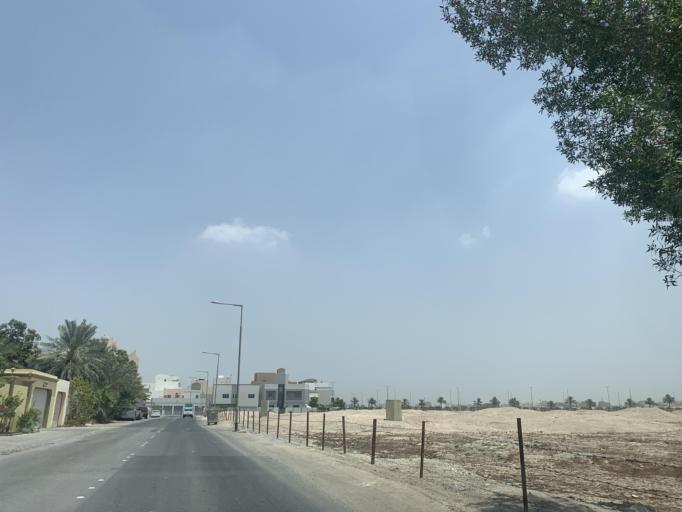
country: BH
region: Central Governorate
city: Madinat Hamad
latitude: 26.1483
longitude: 50.5051
